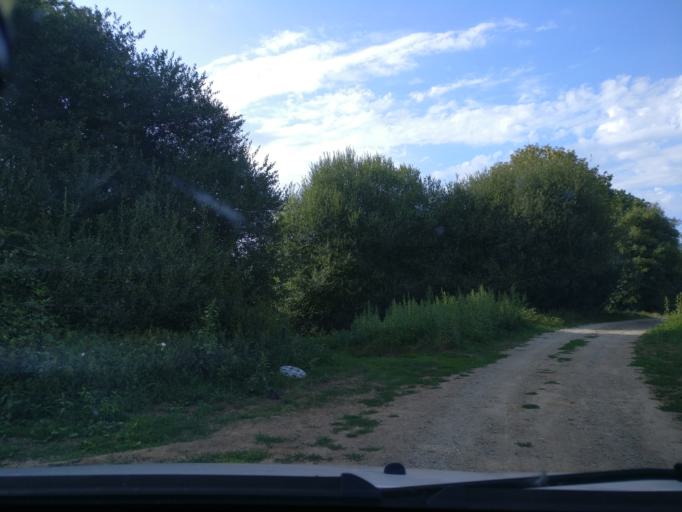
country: FR
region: Brittany
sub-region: Departement d'Ille-et-Vilaine
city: Fouillard
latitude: 48.1360
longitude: -1.5797
